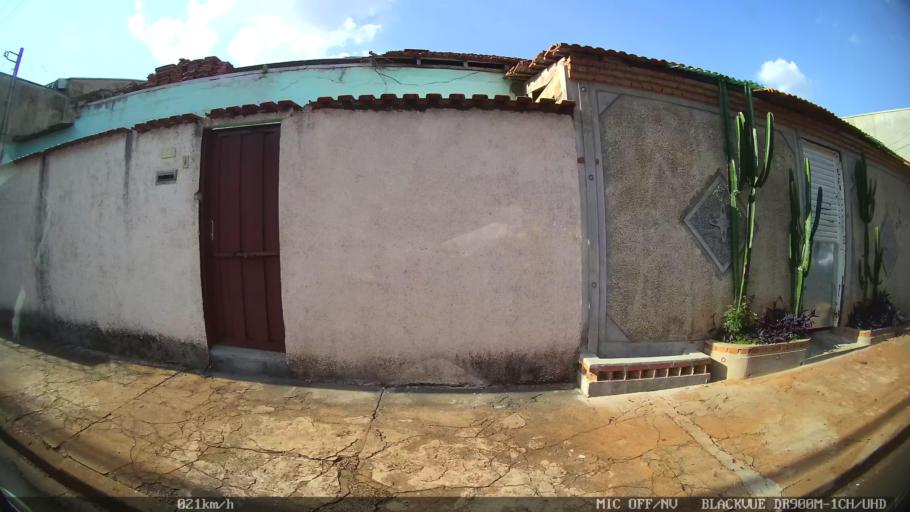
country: BR
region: Sao Paulo
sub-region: Ribeirao Preto
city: Ribeirao Preto
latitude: -21.1677
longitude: -47.8026
